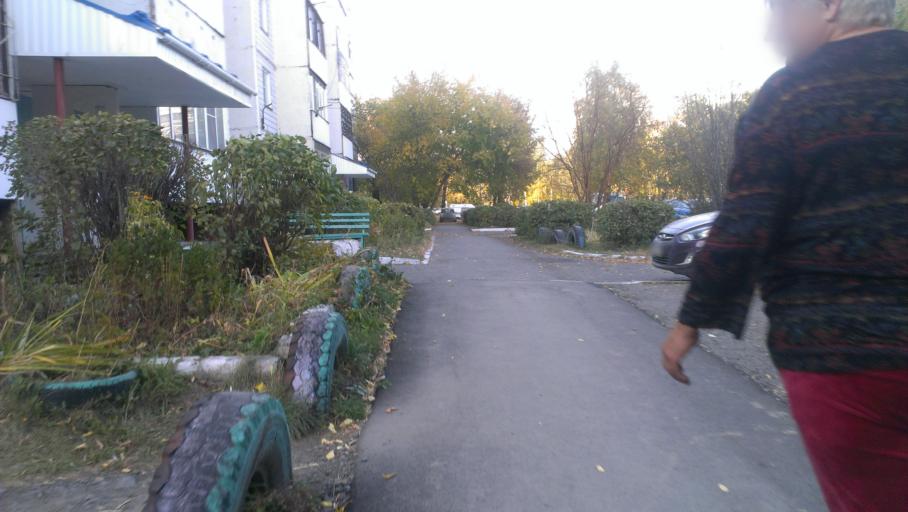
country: RU
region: Altai Krai
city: Novosilikatnyy
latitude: 53.3603
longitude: 83.6812
